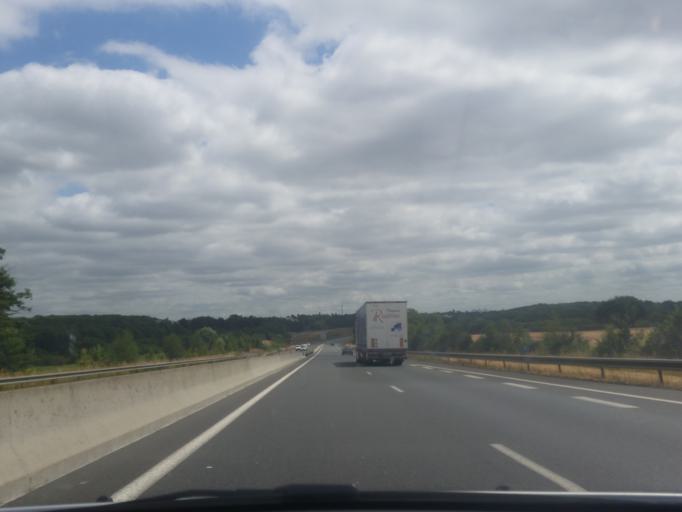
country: FR
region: Pays de la Loire
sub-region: Departement de Maine-et-Loire
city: Beaucouze
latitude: 47.4945
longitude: -0.6156
